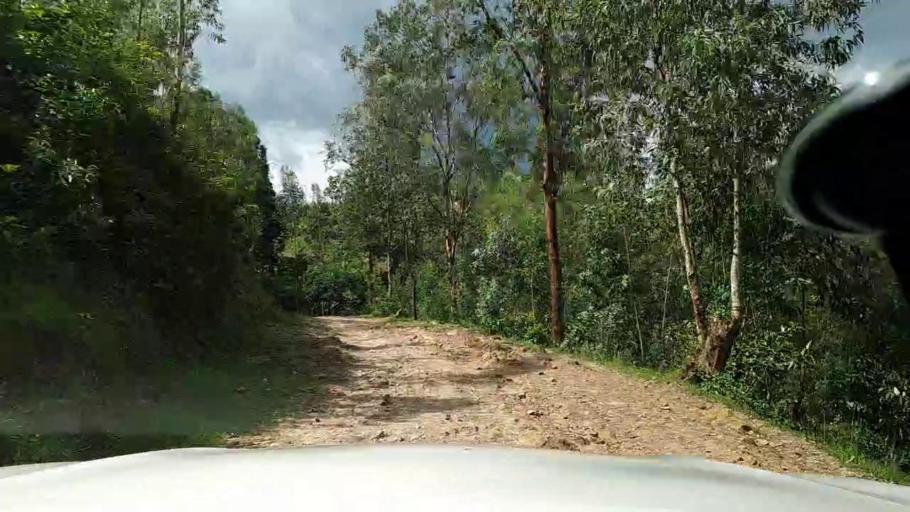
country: RW
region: Southern Province
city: Gitarama
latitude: -1.8232
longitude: 29.8011
